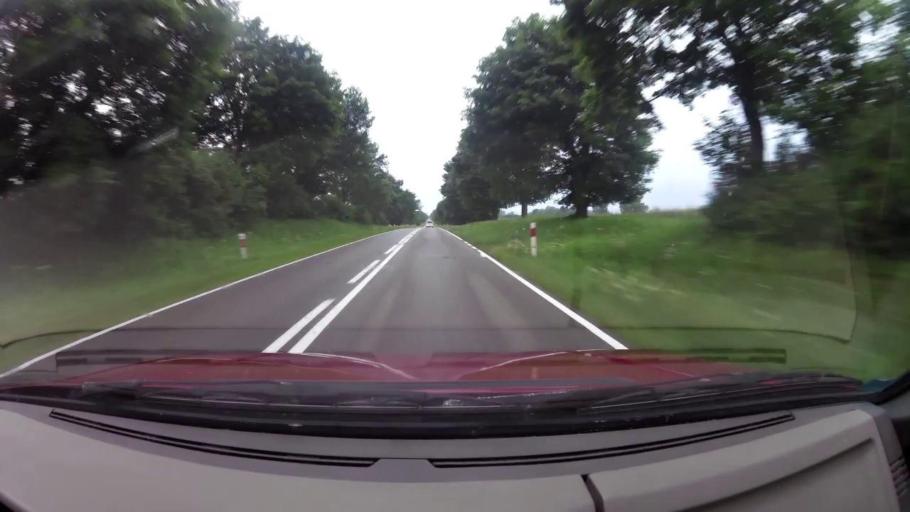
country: PL
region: West Pomeranian Voivodeship
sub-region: Powiat stargardzki
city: Stara Dabrowa
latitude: 53.3895
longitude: 15.1883
